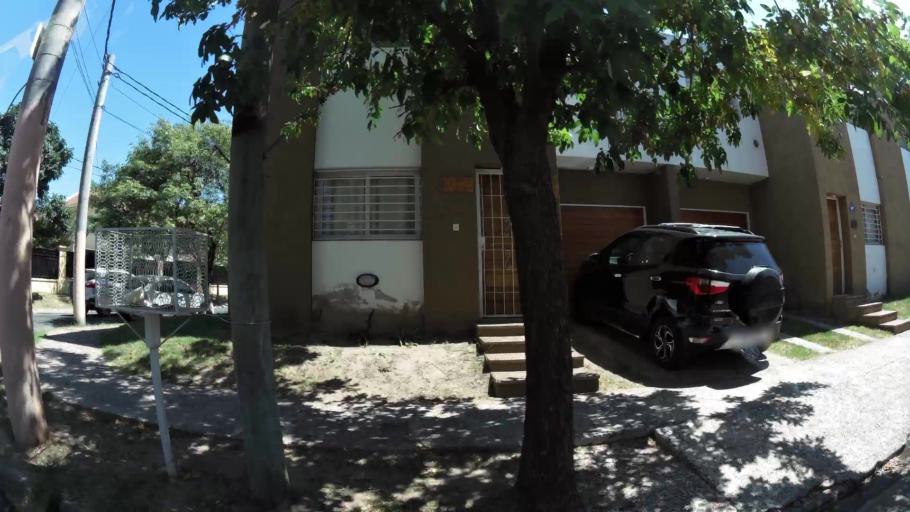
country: AR
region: Cordoba
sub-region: Departamento de Capital
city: Cordoba
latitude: -31.4579
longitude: -64.1628
